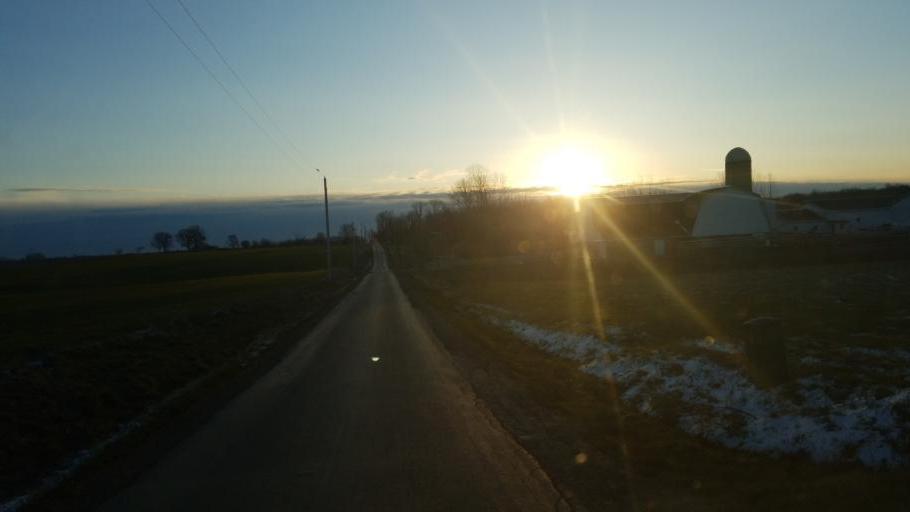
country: US
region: Ohio
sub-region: Highland County
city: Leesburg
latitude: 39.2850
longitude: -83.5088
